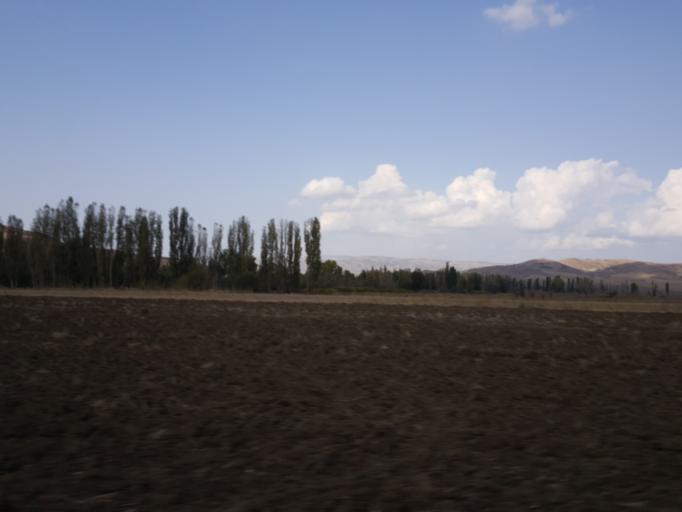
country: TR
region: Corum
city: Bogazkale
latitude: 40.1291
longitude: 34.5368
